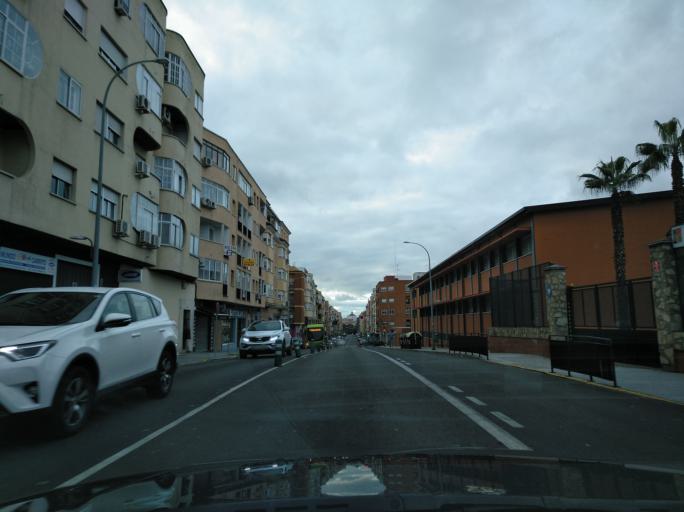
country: ES
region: Extremadura
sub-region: Provincia de Badajoz
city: Badajoz
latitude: 38.8754
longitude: -6.9547
